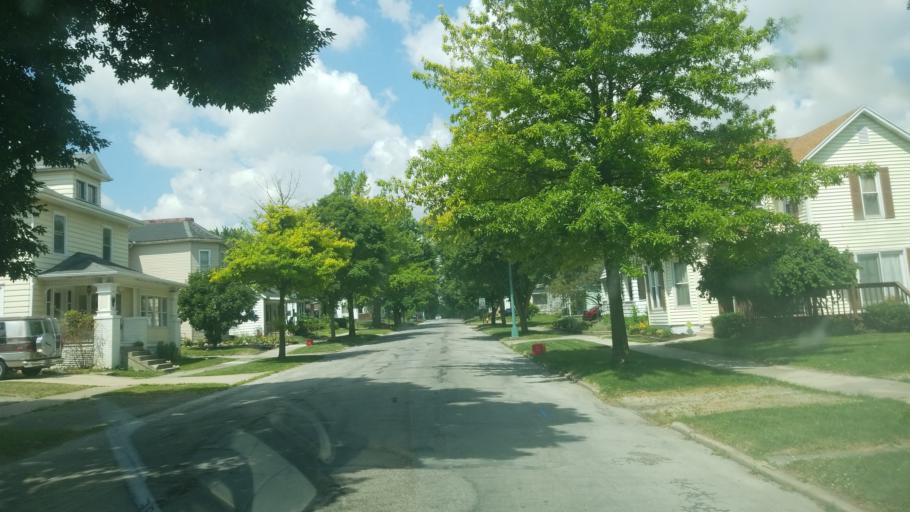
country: US
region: Ohio
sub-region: Auglaize County
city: Wapakoneta
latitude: 40.5669
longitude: -84.1966
